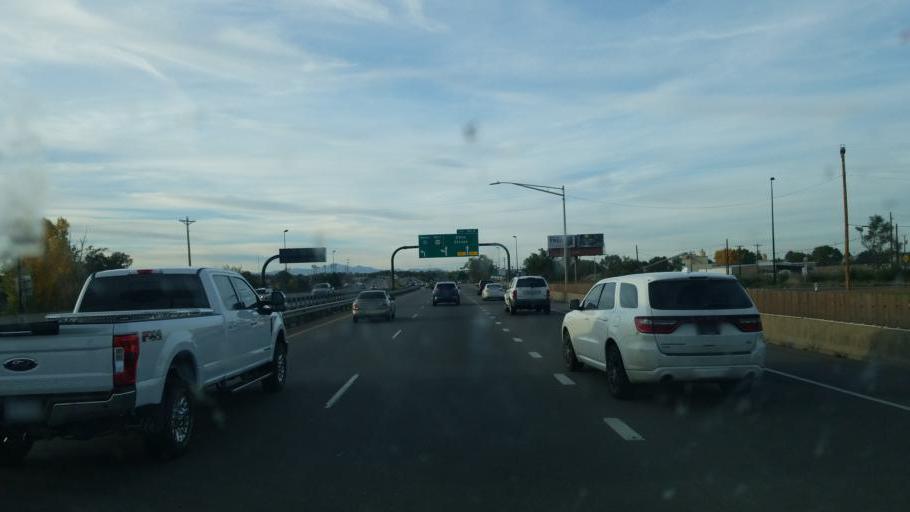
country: US
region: Colorado
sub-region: Pueblo County
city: Pueblo
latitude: 38.2930
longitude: -104.6086
